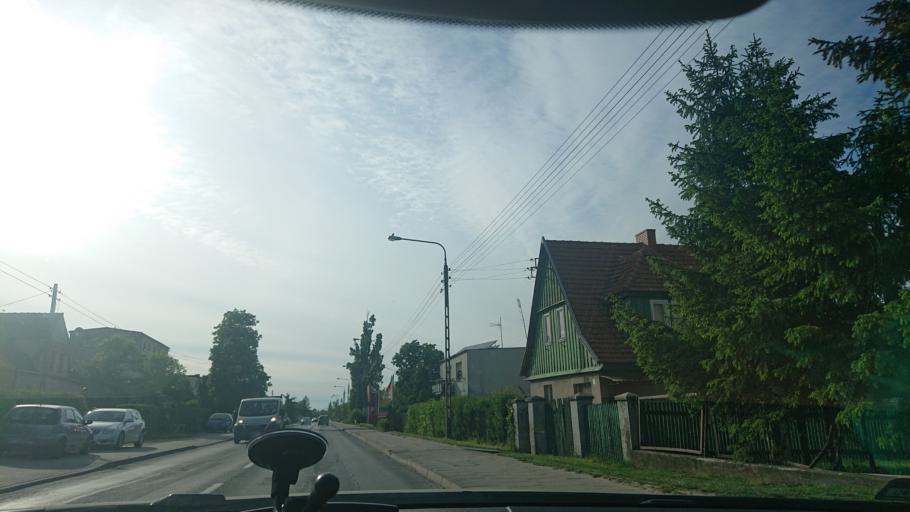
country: PL
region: Greater Poland Voivodeship
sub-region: Powiat gnieznienski
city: Gniezno
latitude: 52.5407
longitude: 17.5806
